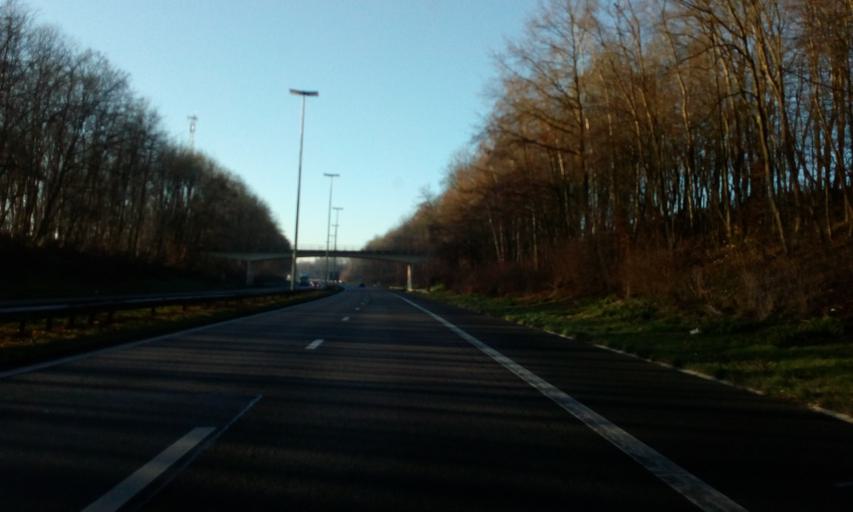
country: BE
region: Wallonia
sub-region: Province du Brabant Wallon
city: Nivelles
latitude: 50.5630
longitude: 4.3410
